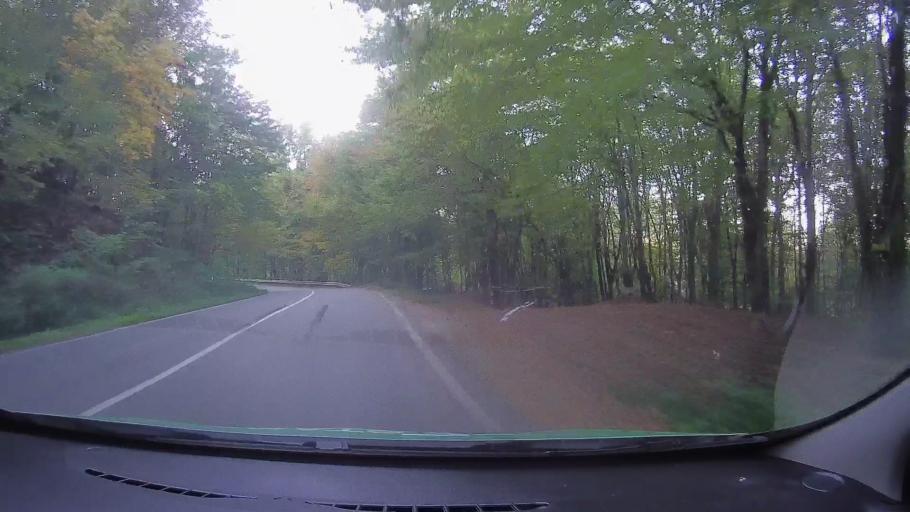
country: RO
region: Timis
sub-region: Comuna Fardea
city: Fardea
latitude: 45.7514
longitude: 22.1268
